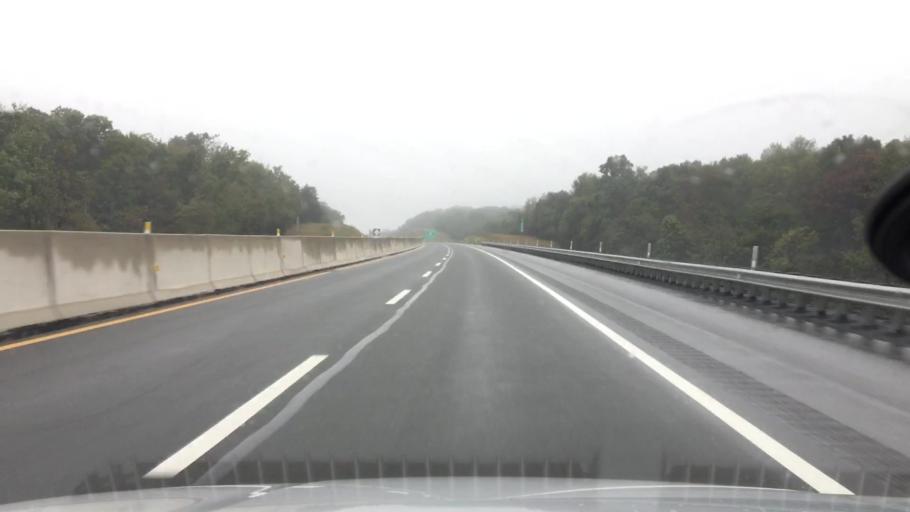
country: US
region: Pennsylvania
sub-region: Luzerne County
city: Mountain Top
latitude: 41.1644
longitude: -75.7750
